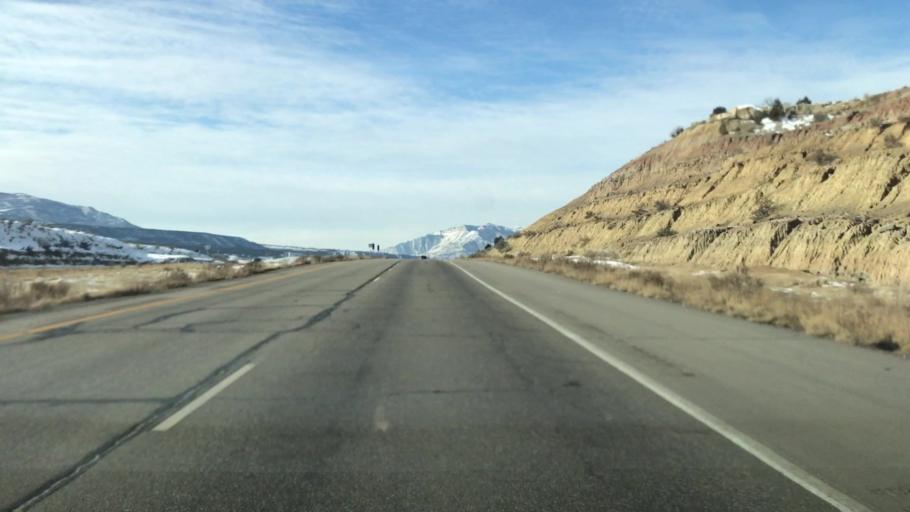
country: US
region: Colorado
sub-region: Garfield County
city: Rifle
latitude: 39.5091
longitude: -107.8798
